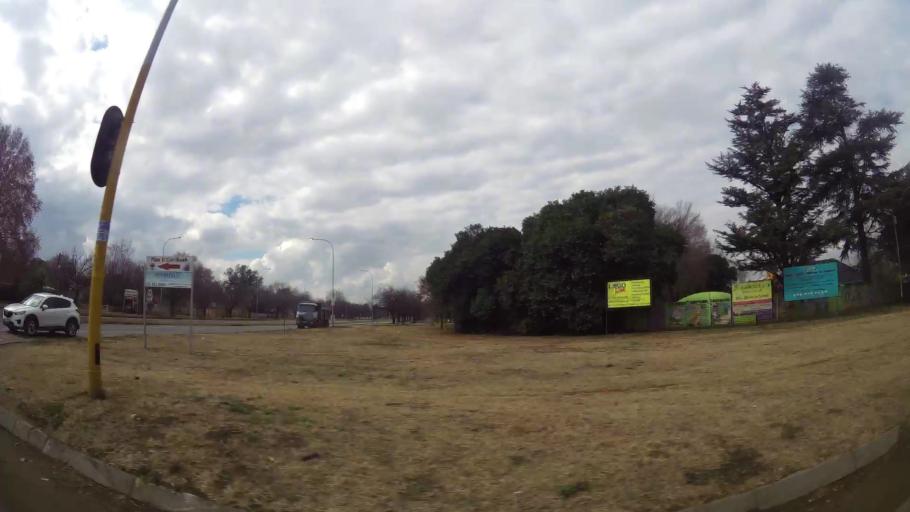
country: ZA
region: Gauteng
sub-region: Sedibeng District Municipality
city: Vereeniging
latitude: -26.6467
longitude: 27.9701
